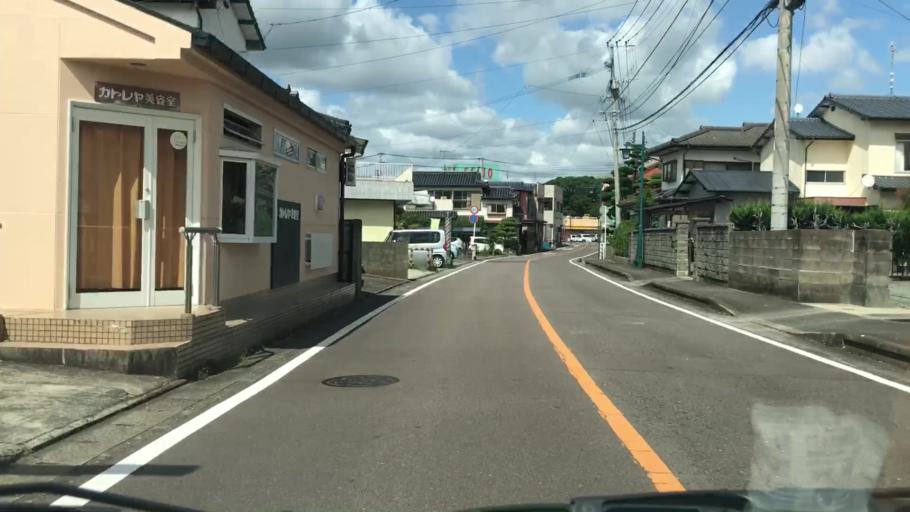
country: JP
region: Saga Prefecture
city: Saga-shi
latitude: 33.2469
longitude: 130.2037
